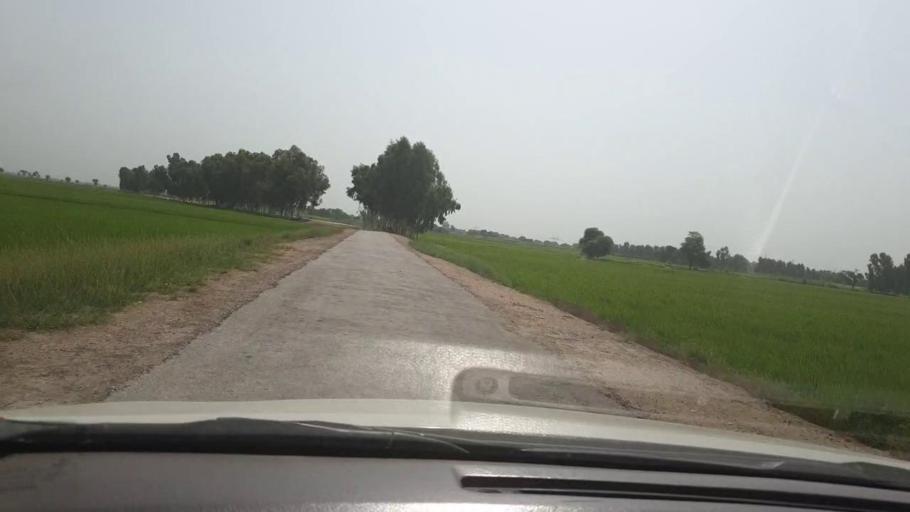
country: PK
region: Sindh
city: Rustam jo Goth
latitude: 27.9748
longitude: 68.7859
